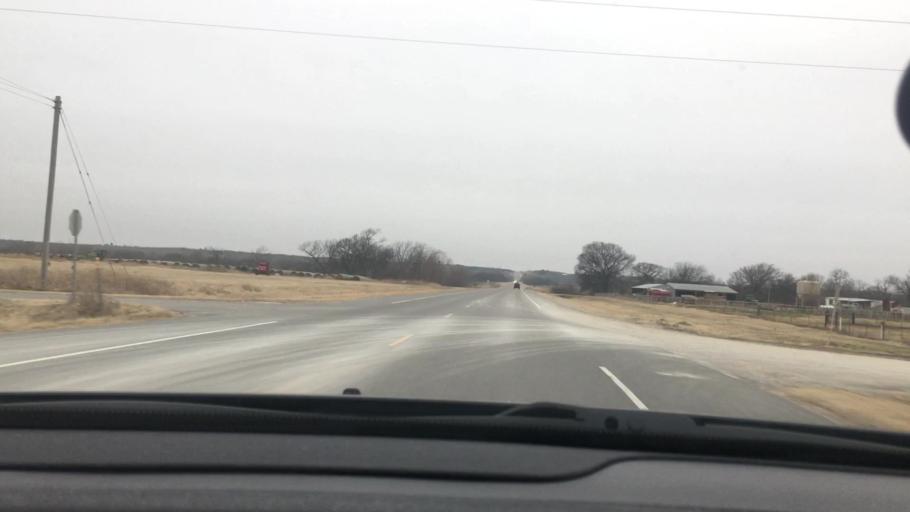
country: US
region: Oklahoma
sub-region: Garvin County
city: Wynnewood
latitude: 34.6226
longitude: -97.1772
